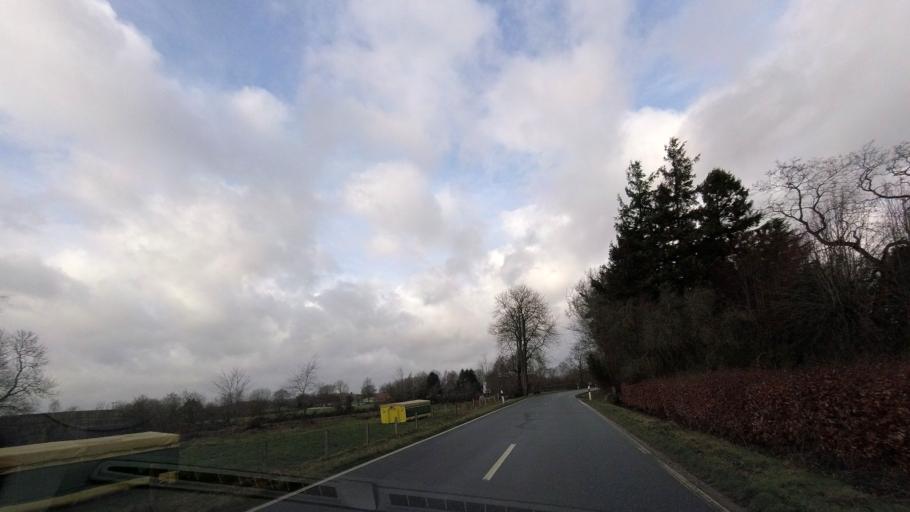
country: DE
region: Schleswig-Holstein
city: Rabenkirchen-Fauluck
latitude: 54.6348
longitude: 9.8745
